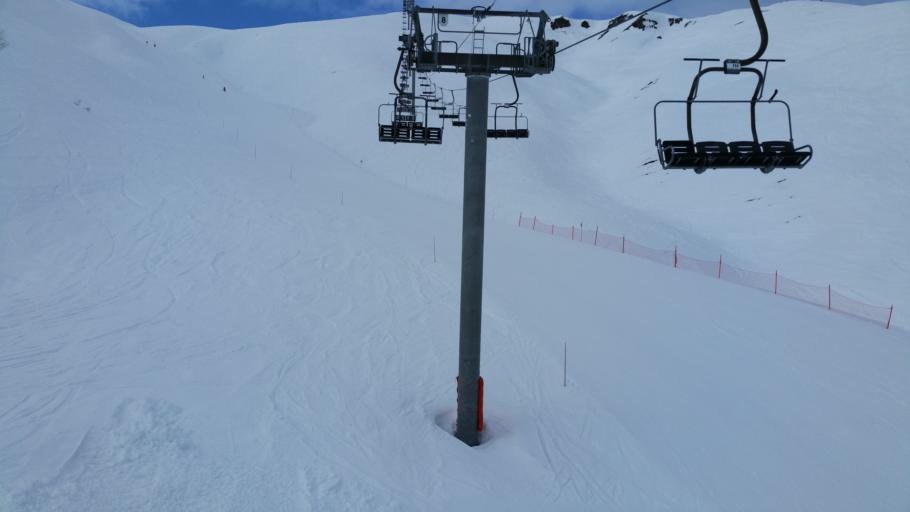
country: FR
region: Rhone-Alpes
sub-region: Departement de la Savoie
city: Saint-Etienne-de-Cuines
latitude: 45.2679
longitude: 6.2615
